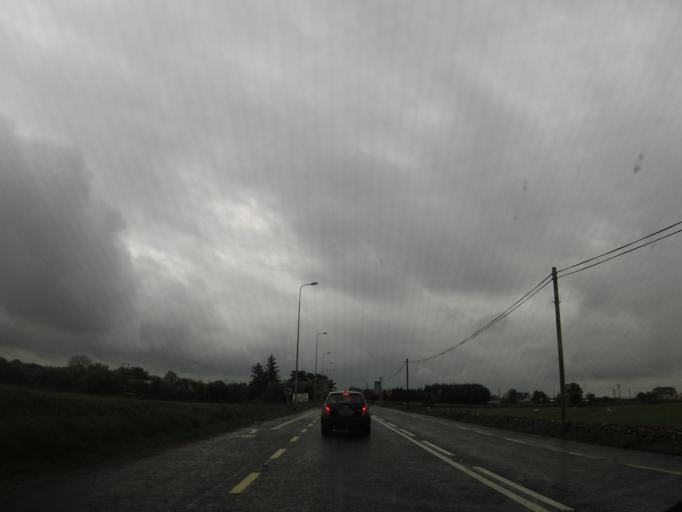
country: IE
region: Connaught
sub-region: County Galway
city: Claregalway
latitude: 53.3927
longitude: -8.9139
